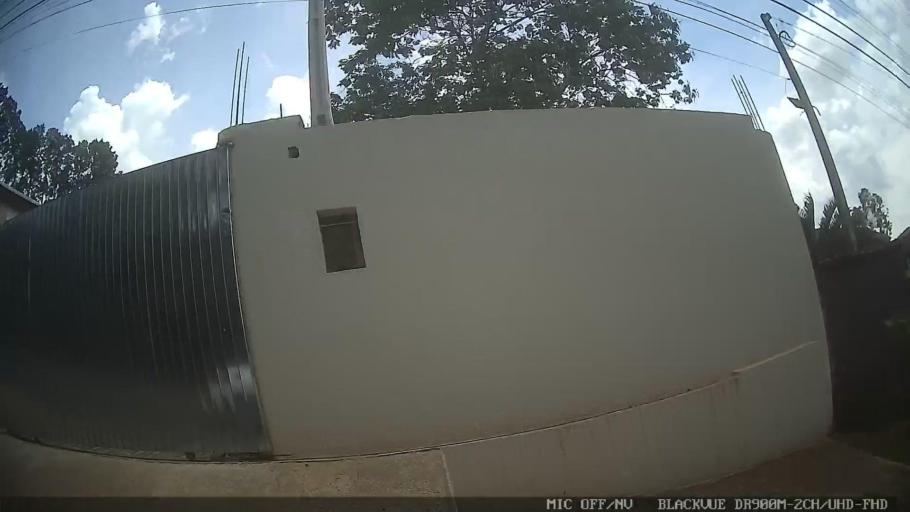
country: BR
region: Sao Paulo
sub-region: Braganca Paulista
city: Braganca Paulista
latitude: -23.0286
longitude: -46.5349
